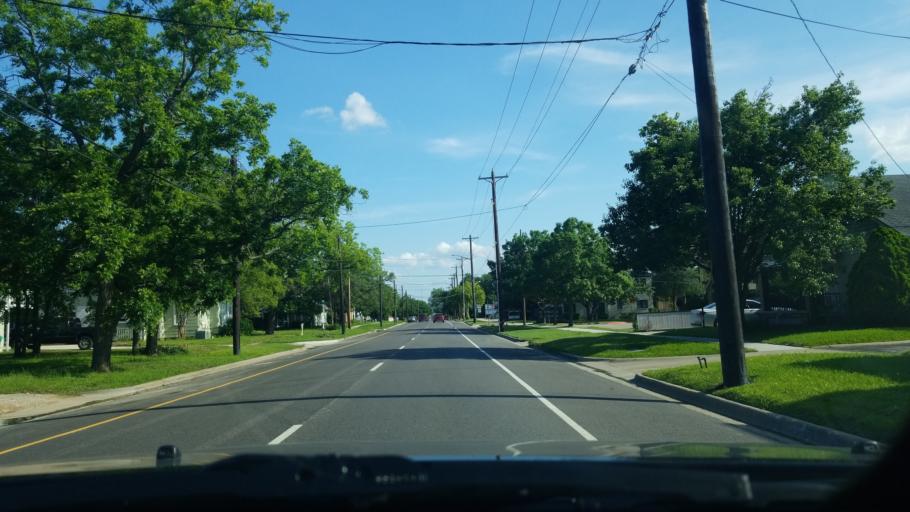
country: US
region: Texas
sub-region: Denton County
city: Denton
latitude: 33.2287
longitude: -97.1336
